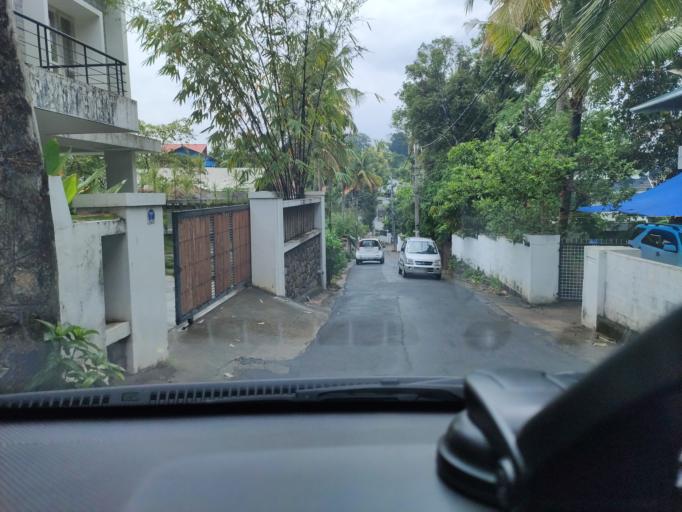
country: IN
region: Kerala
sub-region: Ernakulam
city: Elur
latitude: 10.0276
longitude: 76.3297
